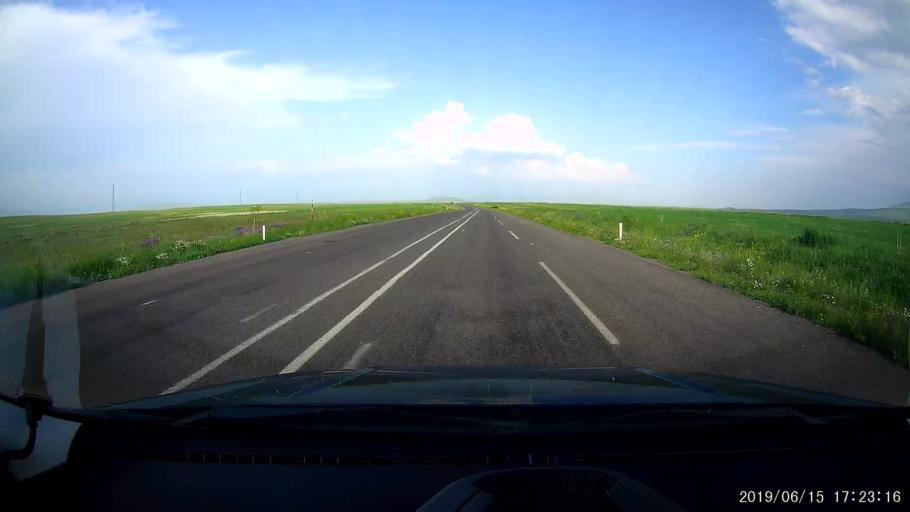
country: TR
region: Kars
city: Basgedikler
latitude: 40.6171
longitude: 43.3595
